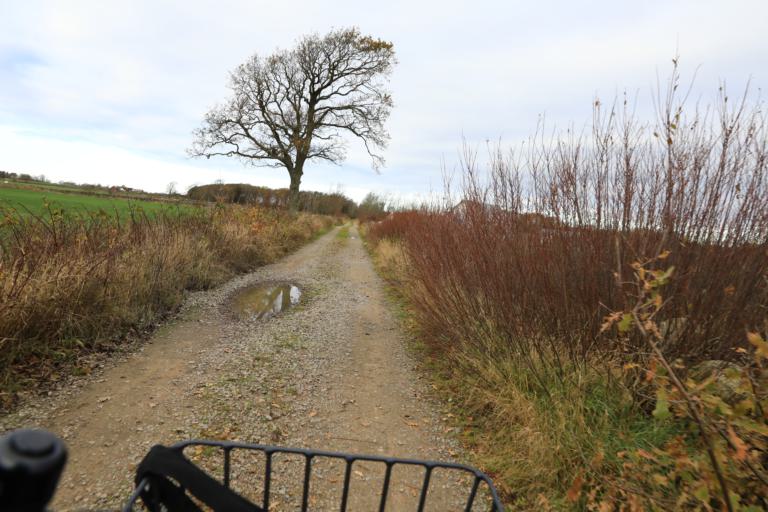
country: SE
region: Halland
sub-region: Varbergs Kommun
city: Traslovslage
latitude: 57.0571
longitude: 12.3349
